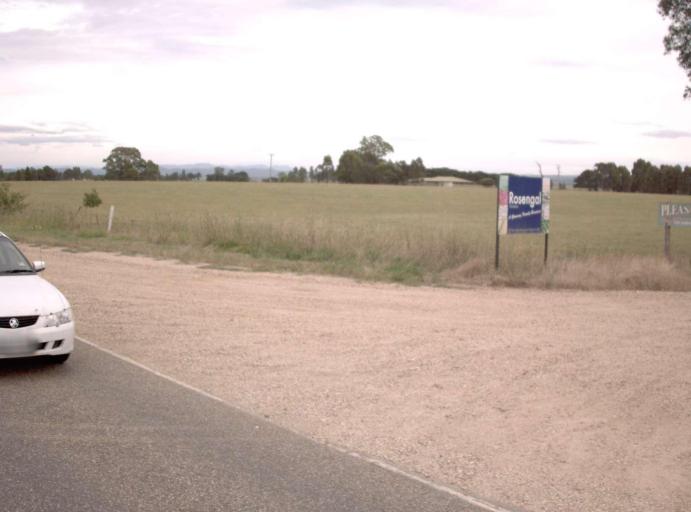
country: AU
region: Victoria
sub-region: East Gippsland
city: Bairnsdale
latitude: -37.8261
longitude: 147.5143
